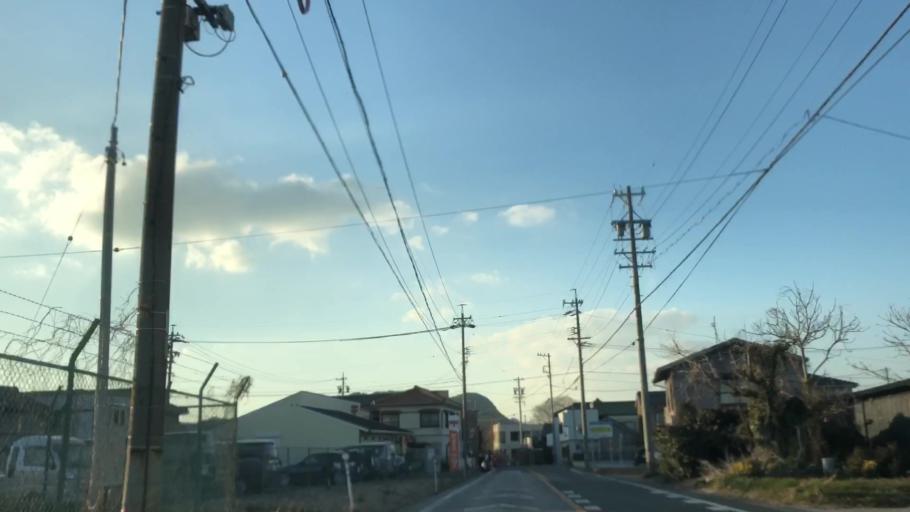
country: JP
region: Aichi
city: Tahara
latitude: 34.6545
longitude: 137.2075
